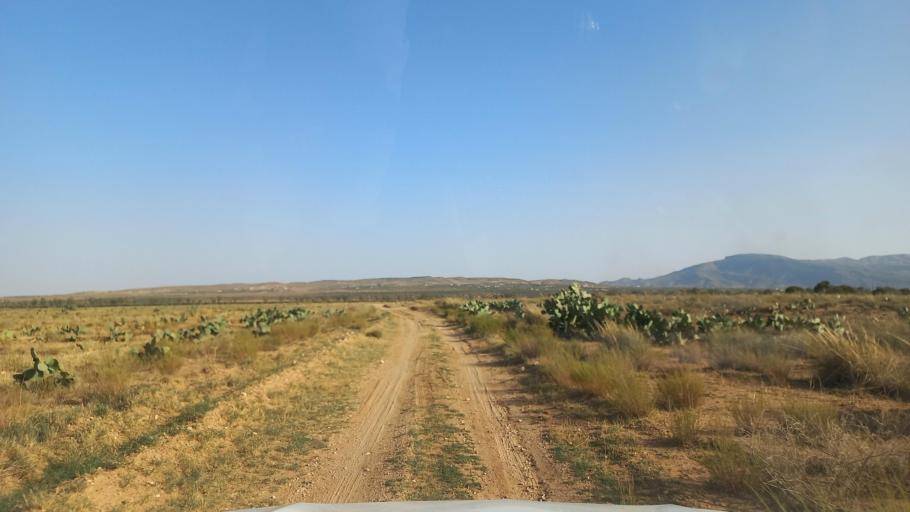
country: TN
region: Al Qasrayn
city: Kasserine
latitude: 35.2336
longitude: 8.9378
